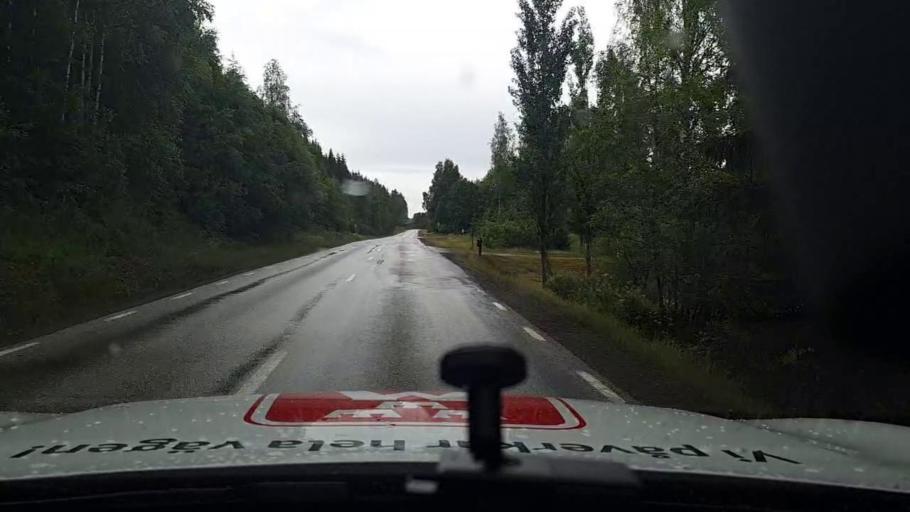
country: SE
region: Vaermland
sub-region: Torsby Kommun
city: Torsby
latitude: 60.4521
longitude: 13.2252
